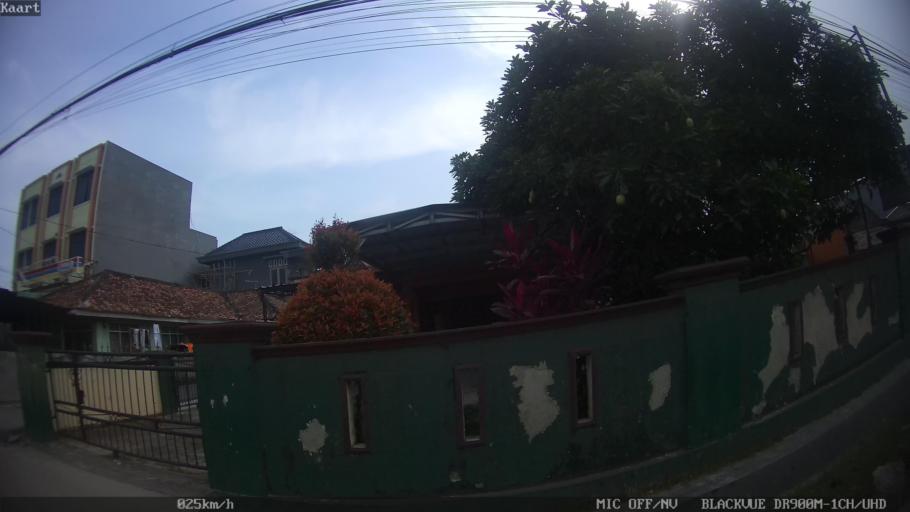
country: ID
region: Lampung
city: Kedaton
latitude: -5.3982
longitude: 105.3049
